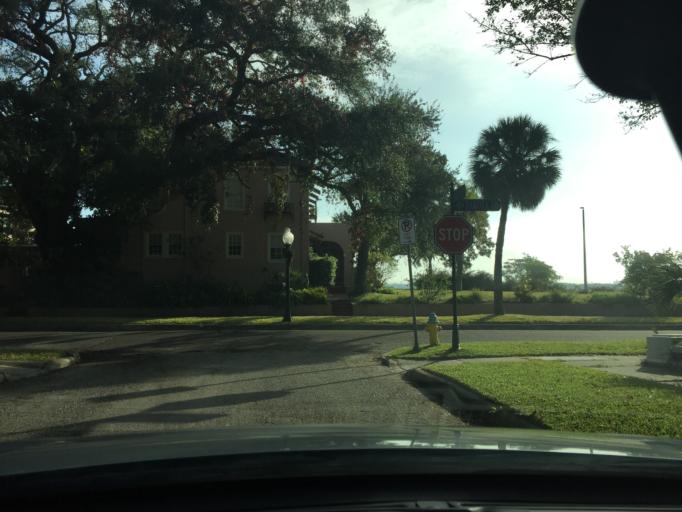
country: US
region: Florida
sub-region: Hillsborough County
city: Tampa
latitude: 27.9304
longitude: -82.4760
